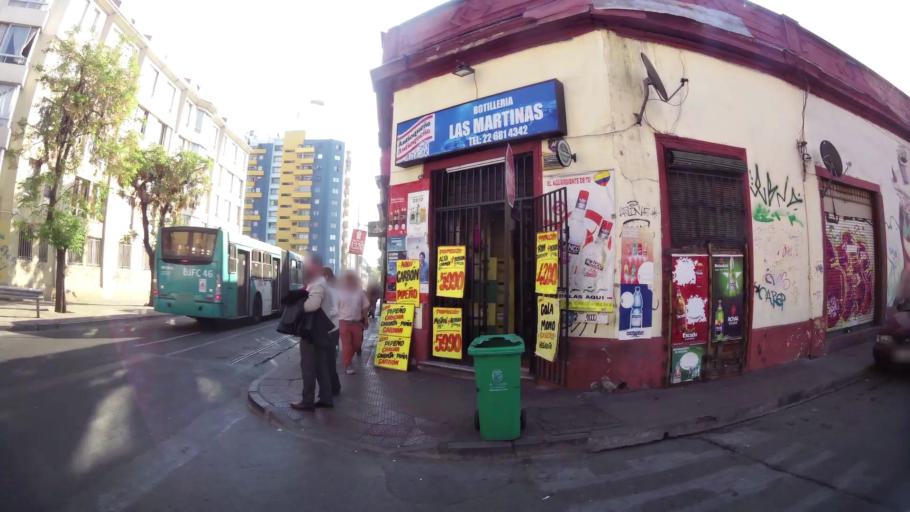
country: CL
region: Santiago Metropolitan
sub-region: Provincia de Santiago
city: Santiago
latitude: -33.4397
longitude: -70.6735
